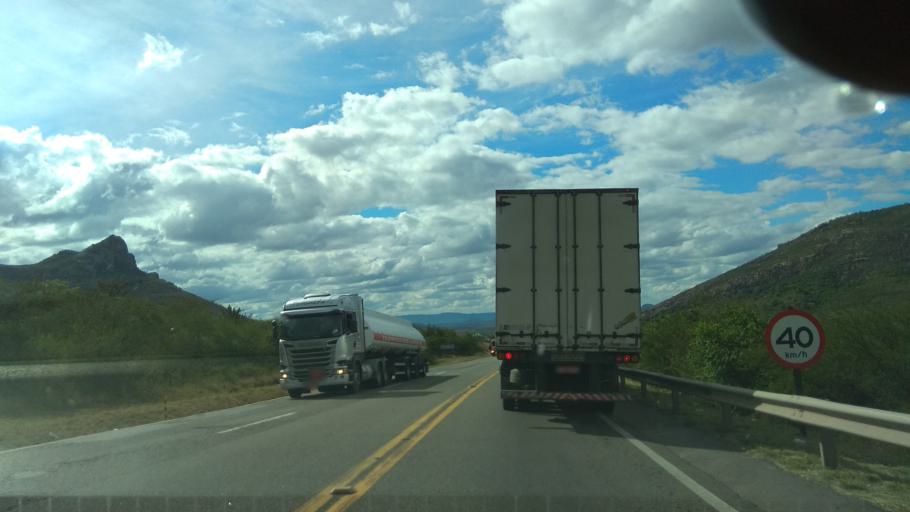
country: BR
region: Bahia
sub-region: Amargosa
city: Amargosa
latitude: -12.8846
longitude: -39.8590
